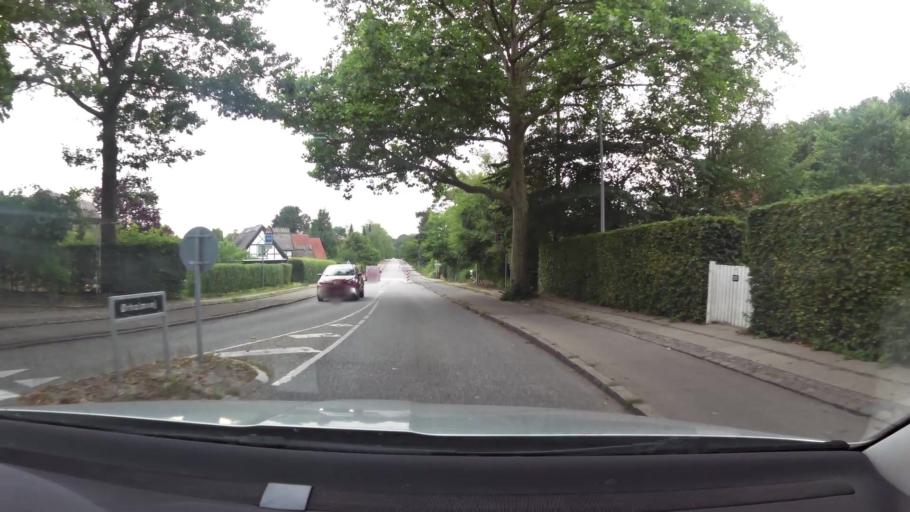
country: DK
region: Capital Region
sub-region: Lyngby-Tarbaek Kommune
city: Kongens Lyngby
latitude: 55.7980
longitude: 12.5139
